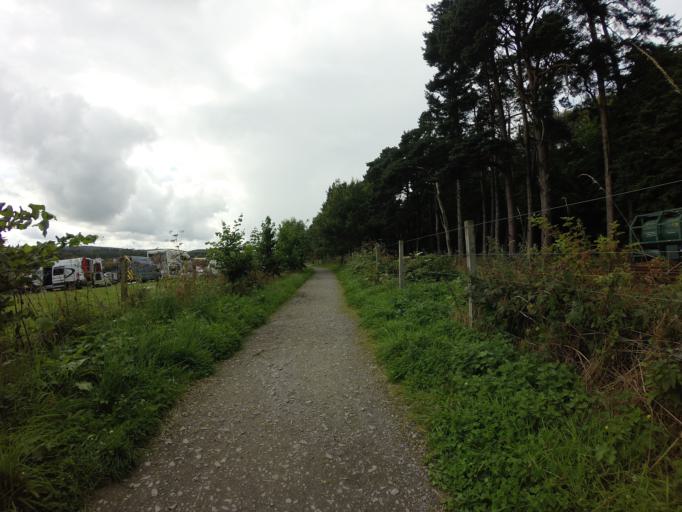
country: GB
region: Scotland
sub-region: Aberdeenshire
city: Banchory
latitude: 57.0560
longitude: -2.4319
